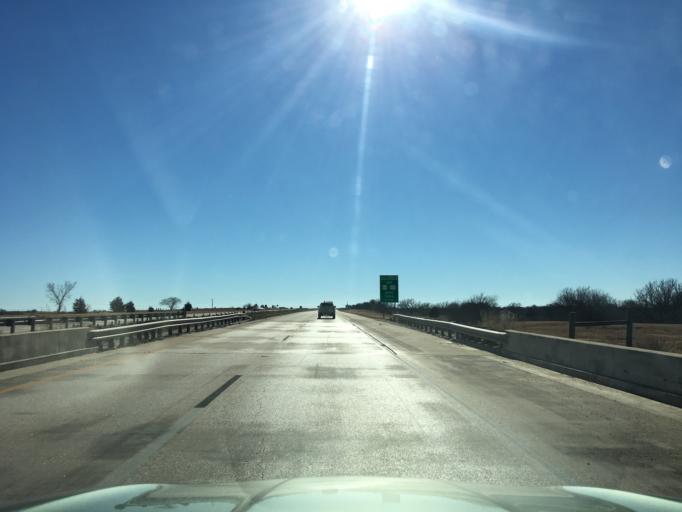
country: US
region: Oklahoma
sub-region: Noble County
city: Perry
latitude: 36.4347
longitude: -97.3271
